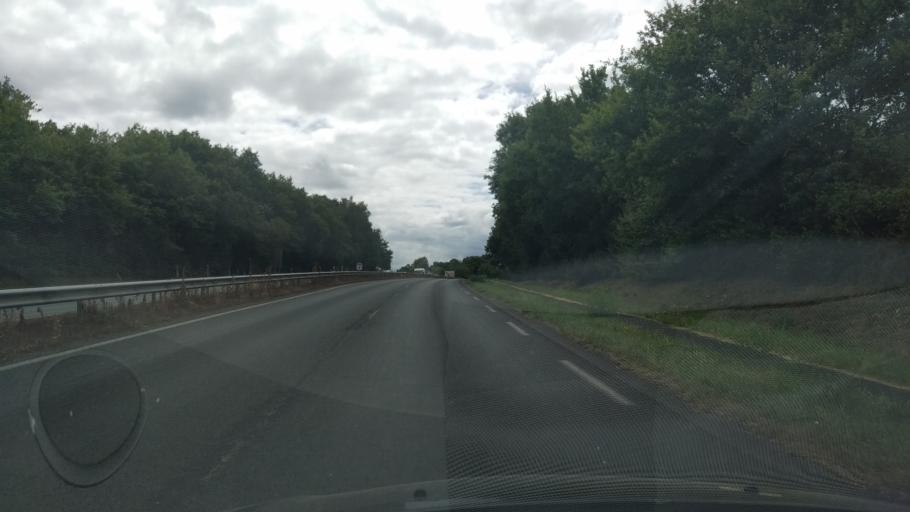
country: FR
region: Poitou-Charentes
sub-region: Departement de la Vienne
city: Saint-Benoit
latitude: 46.5530
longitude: 0.3300
